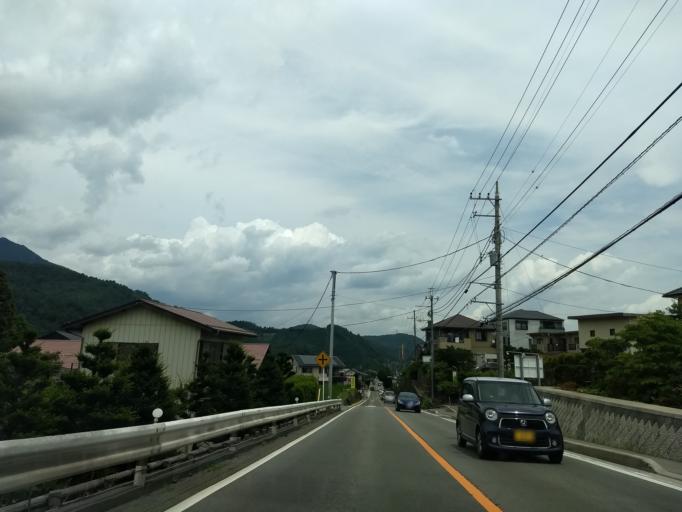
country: JP
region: Yamanashi
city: Otsuki
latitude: 35.5142
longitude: 138.8326
